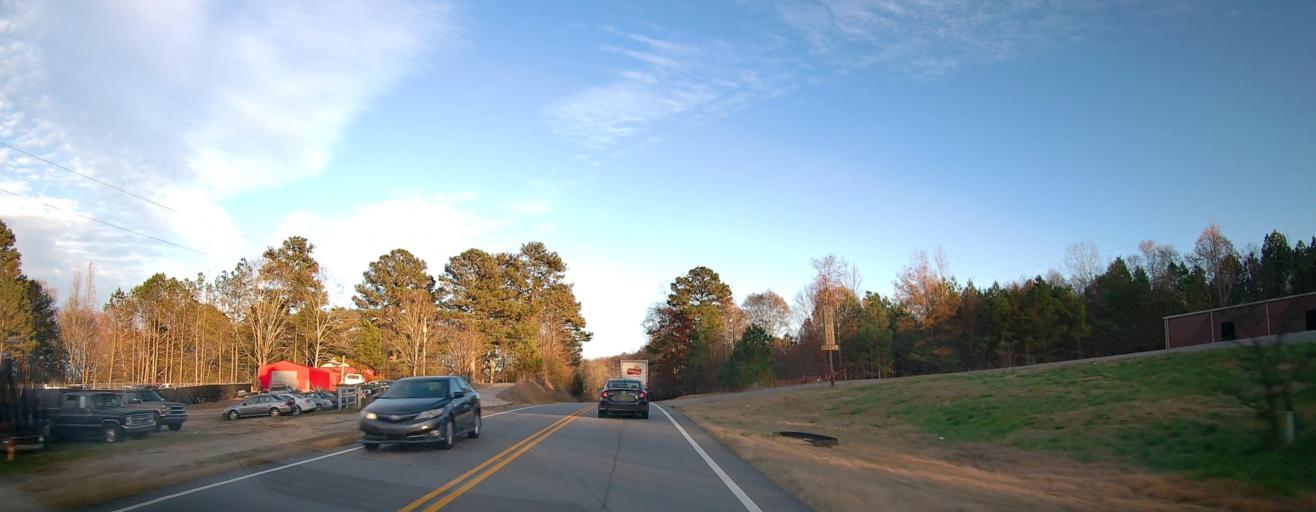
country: US
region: Alabama
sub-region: Saint Clair County
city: Steele
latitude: 34.0722
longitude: -86.3201
